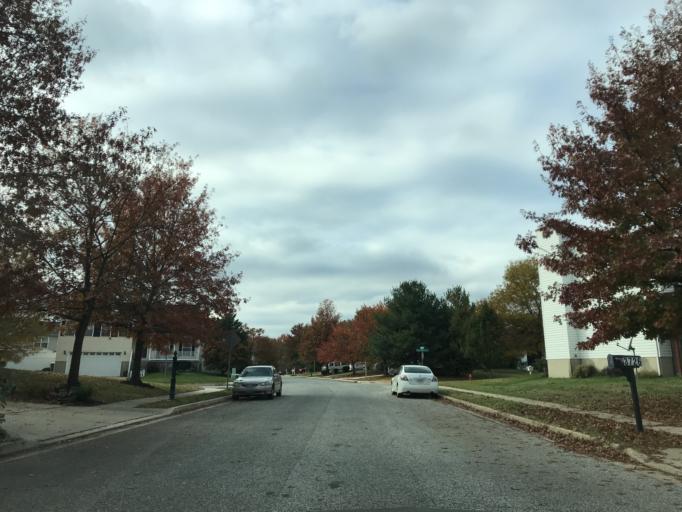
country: US
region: Maryland
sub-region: Baltimore County
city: Bowleys Quarters
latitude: 39.3256
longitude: -76.3911
